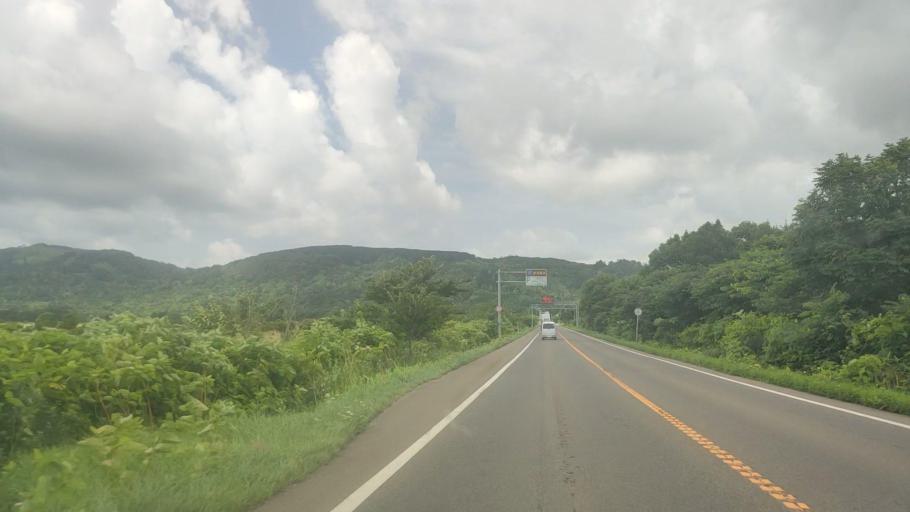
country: JP
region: Hokkaido
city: Niseko Town
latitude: 42.5826
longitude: 140.4529
